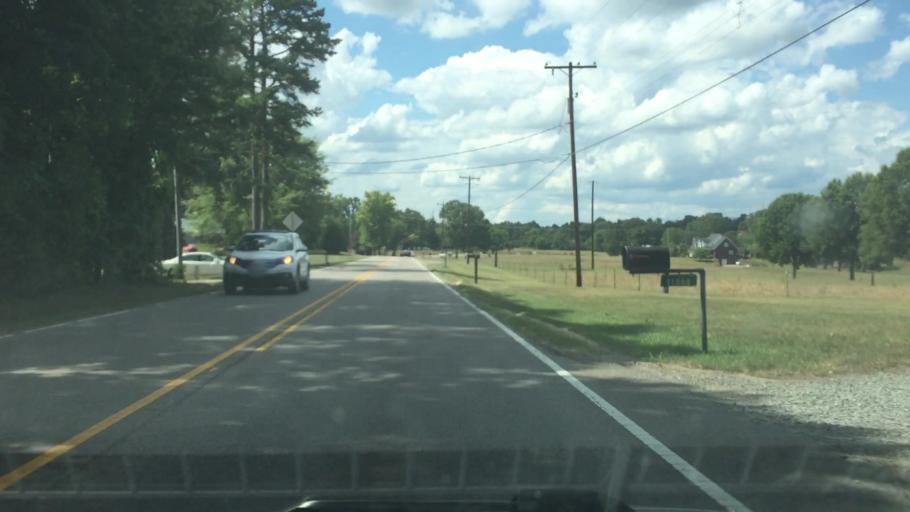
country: US
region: North Carolina
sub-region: Gaston County
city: Davidson
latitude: 35.4941
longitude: -80.7683
